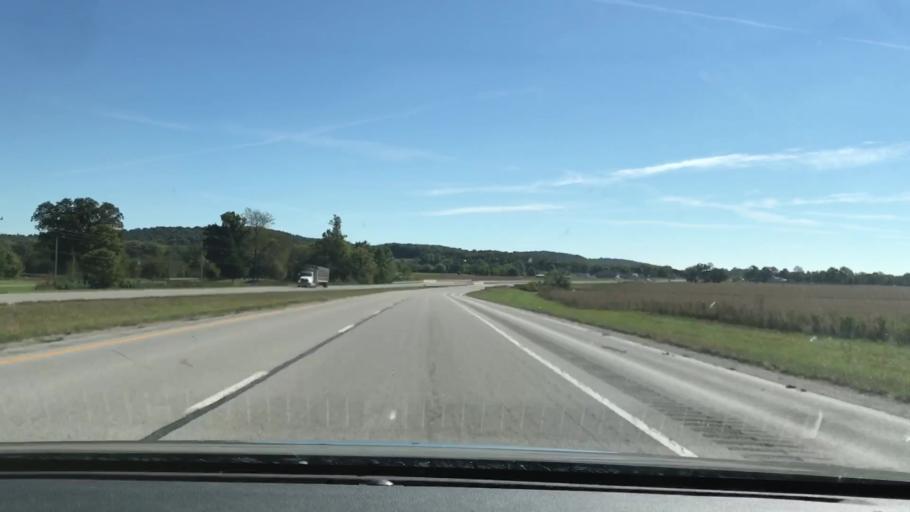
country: US
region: Kentucky
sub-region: Todd County
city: Elkton
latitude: 36.8403
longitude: -87.2490
